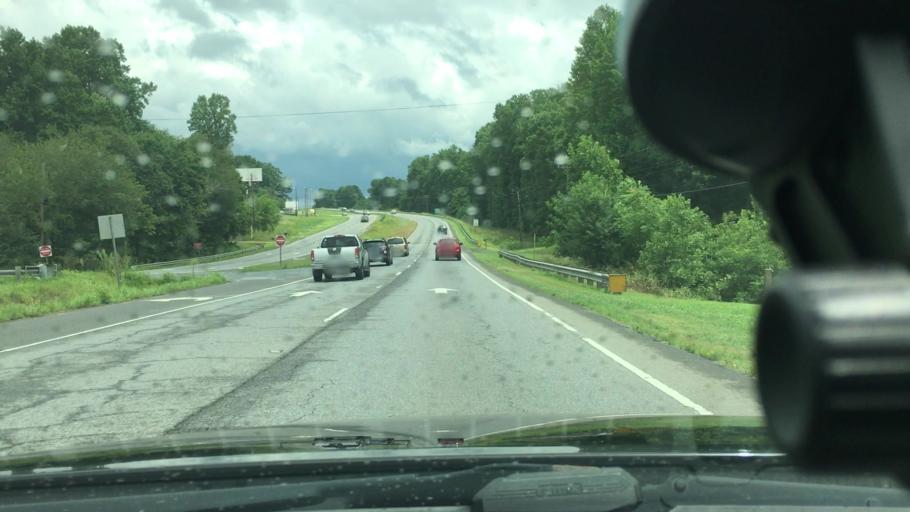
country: US
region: North Carolina
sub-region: Cleveland County
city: Boiling Springs
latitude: 35.2935
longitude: -81.6081
